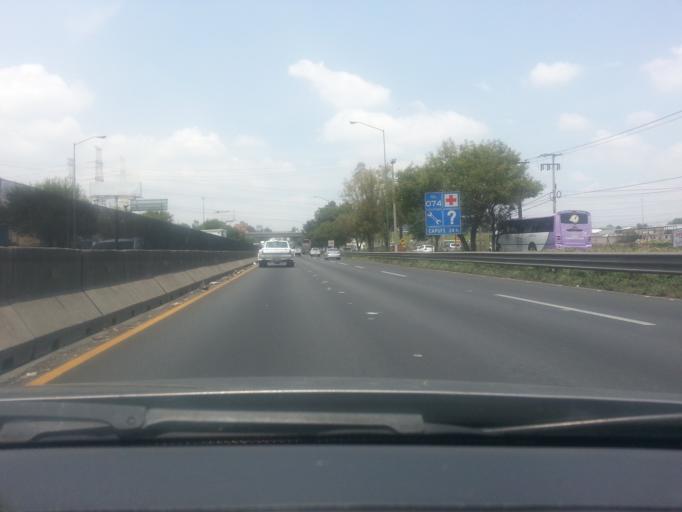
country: MX
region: Mexico
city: Cuautitlan Izcalli
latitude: 19.6335
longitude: -99.1939
